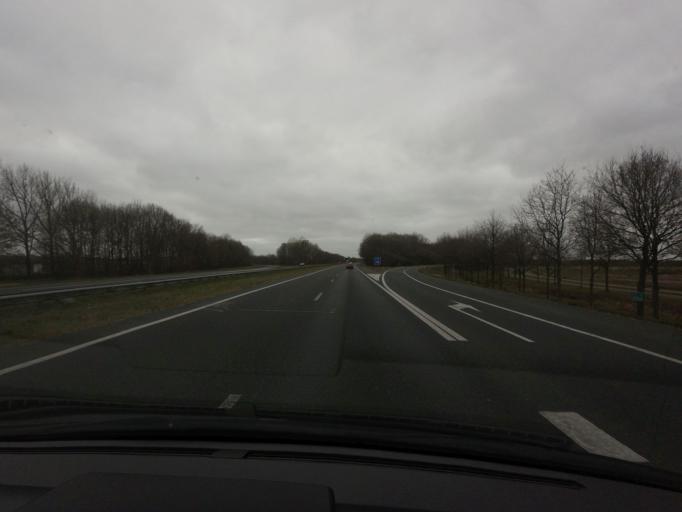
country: NL
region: Groningen
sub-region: Gemeente Hoogezand-Sappemeer
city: Hoogezand
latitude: 53.1691
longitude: 6.7637
